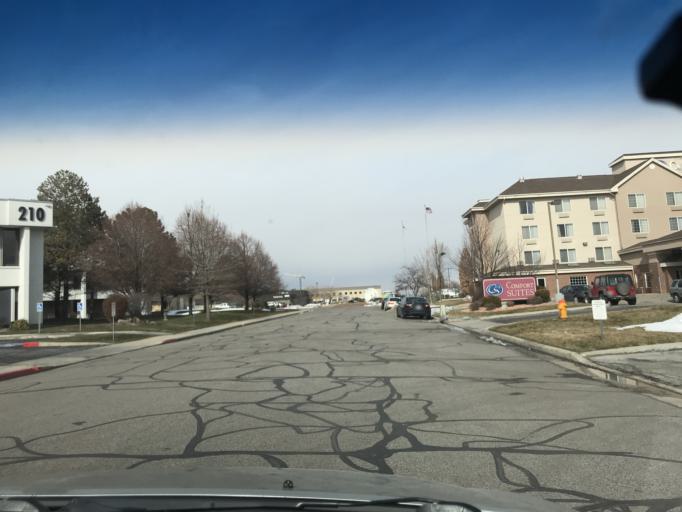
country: US
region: Utah
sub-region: Salt Lake County
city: Salt Lake City
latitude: 40.7727
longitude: -111.9512
